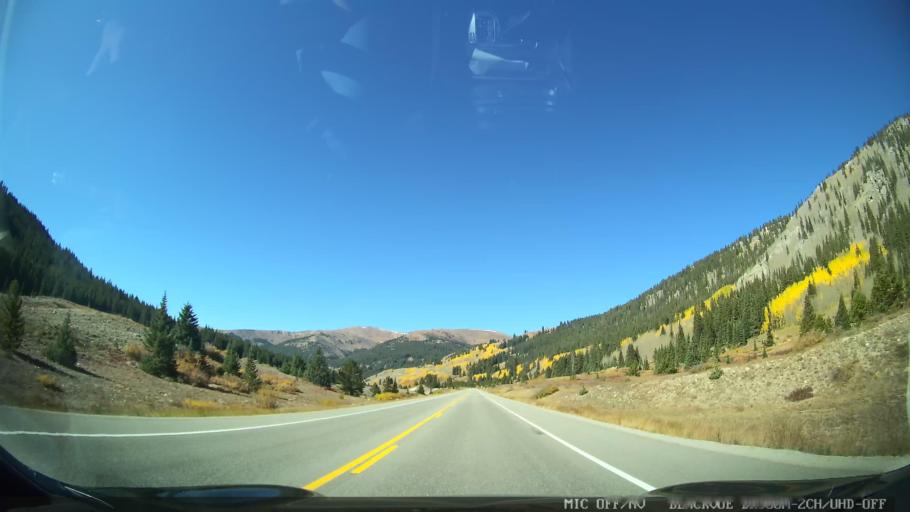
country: US
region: Colorado
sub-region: Lake County
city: Leadville
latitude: 39.3617
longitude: -106.1981
